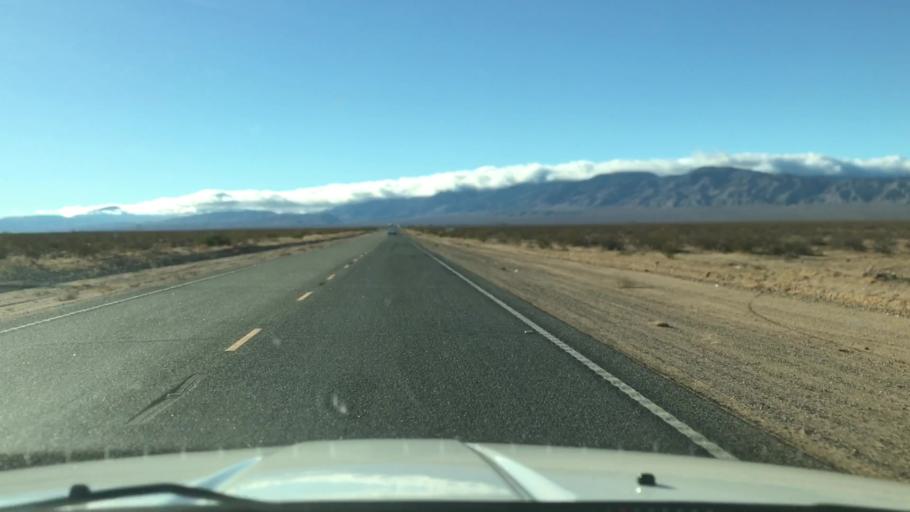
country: US
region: California
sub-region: Kern County
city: California City
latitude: 35.1256
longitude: -118.0438
